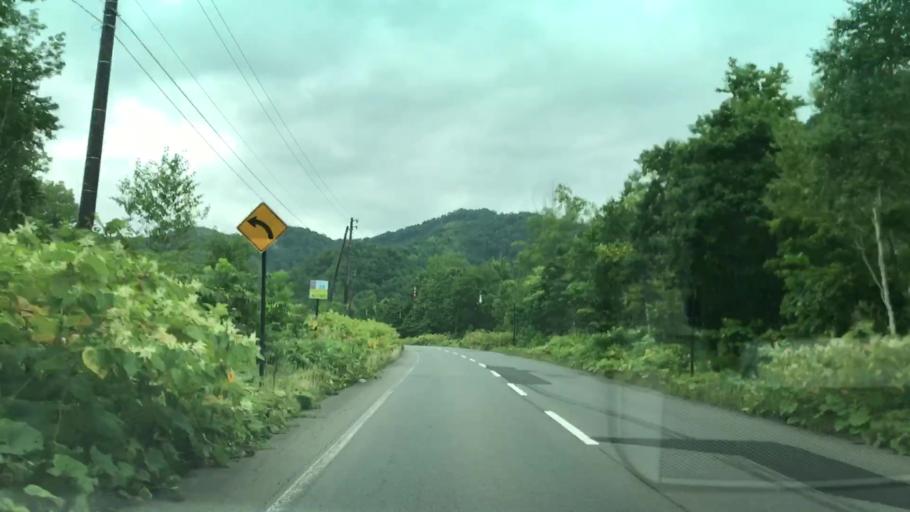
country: JP
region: Hokkaido
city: Yoichi
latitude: 43.0150
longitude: 140.8678
